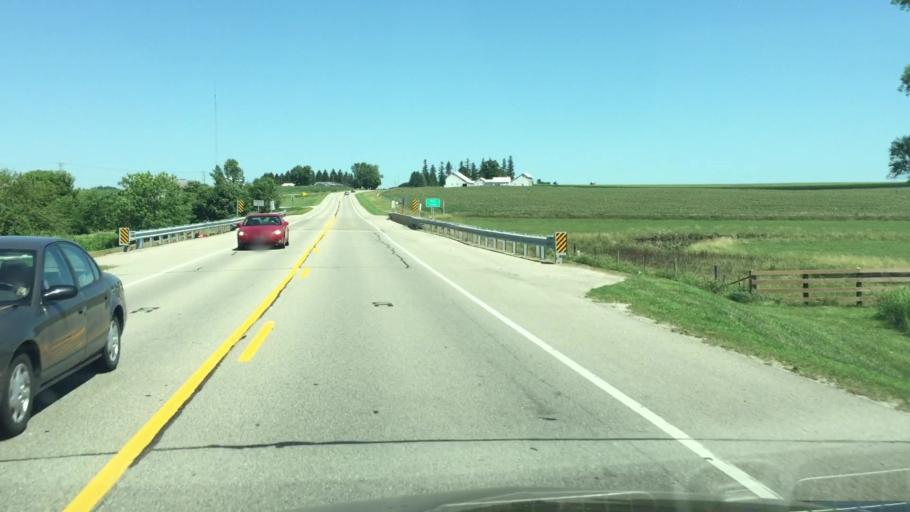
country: US
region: Iowa
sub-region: Johnson County
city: Solon
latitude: 41.8119
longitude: -91.4936
